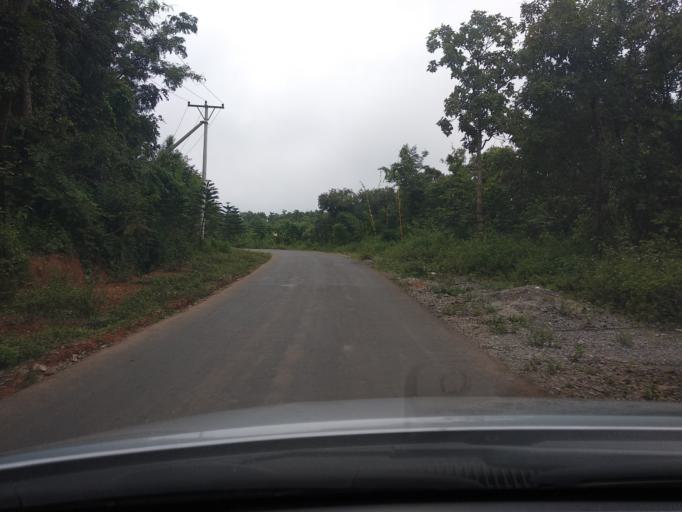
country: MM
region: Mandalay
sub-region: Pyin Oo Lwin District
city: Pyin Oo Lwin
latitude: 21.9230
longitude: 96.3753
